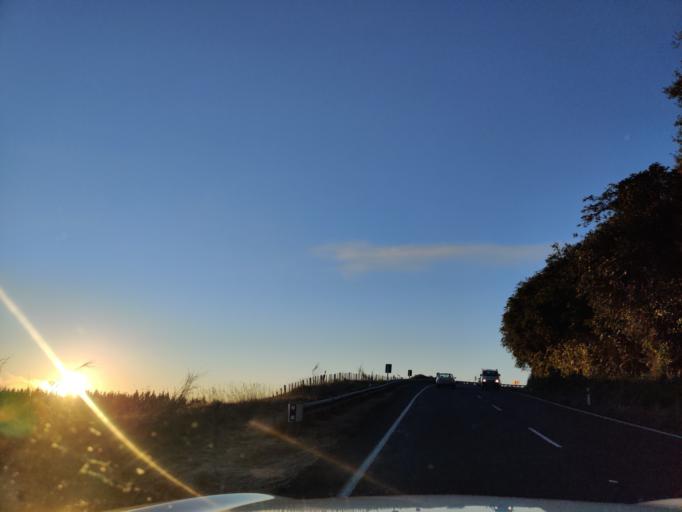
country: NZ
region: Waikato
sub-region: Taupo District
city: Taupo
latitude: -38.6513
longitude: 176.0600
